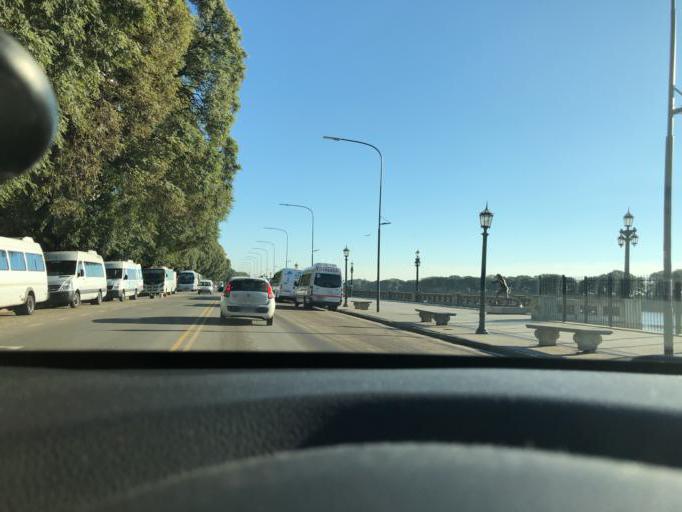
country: AR
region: Buenos Aires F.D.
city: Buenos Aires
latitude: -34.6158
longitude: -58.3571
